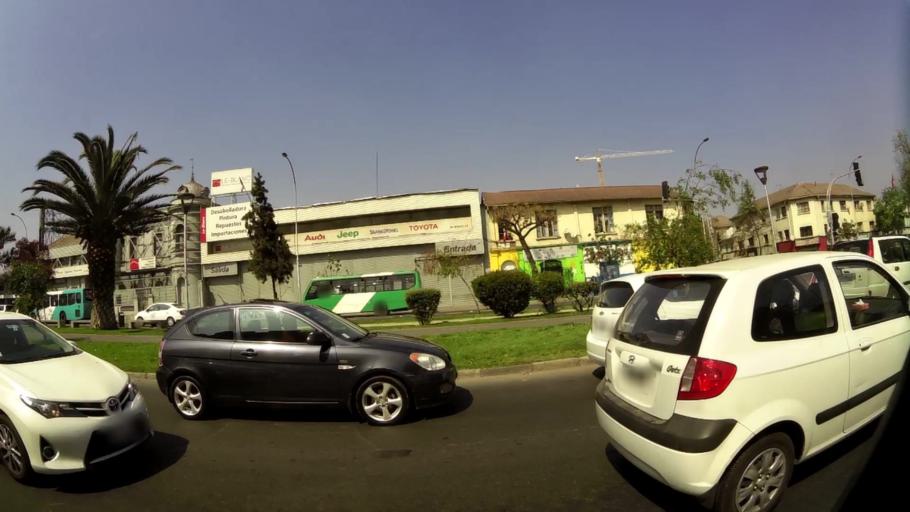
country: CL
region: Santiago Metropolitan
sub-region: Provincia de Santiago
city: Santiago
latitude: -33.4588
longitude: -70.6461
